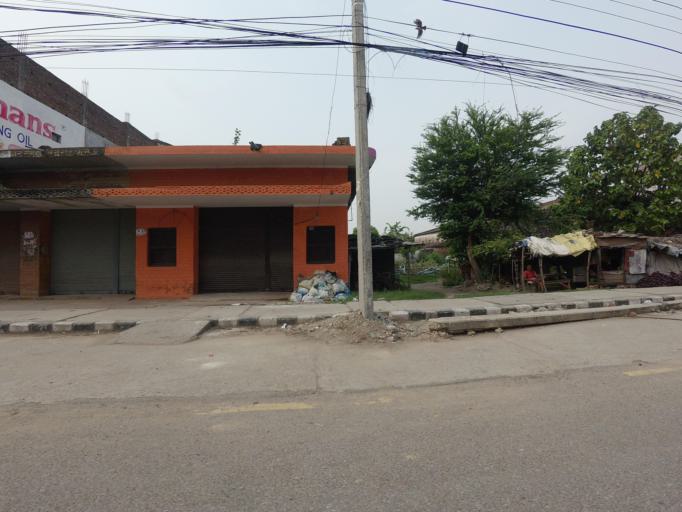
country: NP
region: Western Region
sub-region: Lumbini Zone
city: Bhairahawa
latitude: 27.5072
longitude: 83.4429
